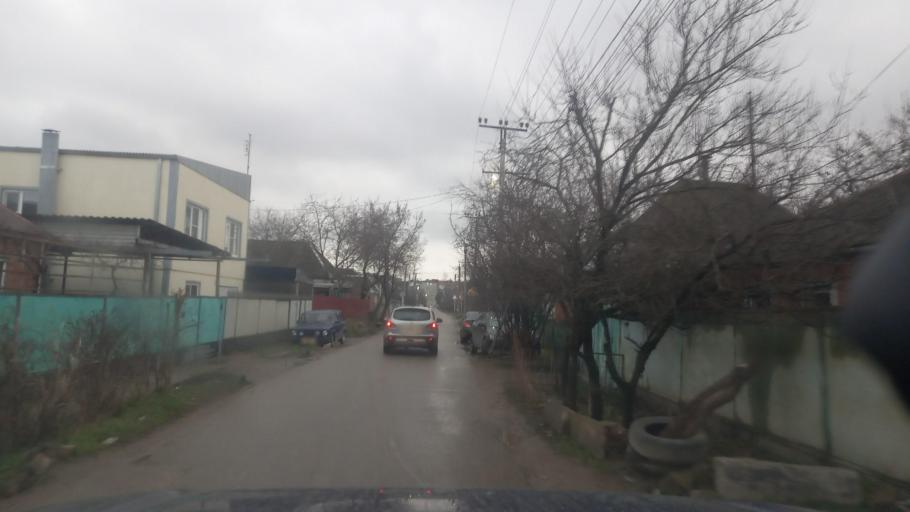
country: RU
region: Adygeya
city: Yablonovskiy
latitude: 44.9763
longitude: 38.9370
